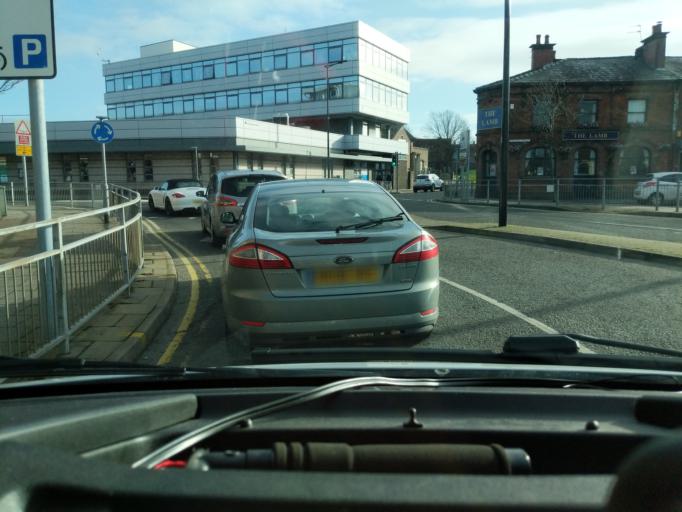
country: GB
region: England
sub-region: St. Helens
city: St Helens
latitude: 53.4554
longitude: -2.7386
